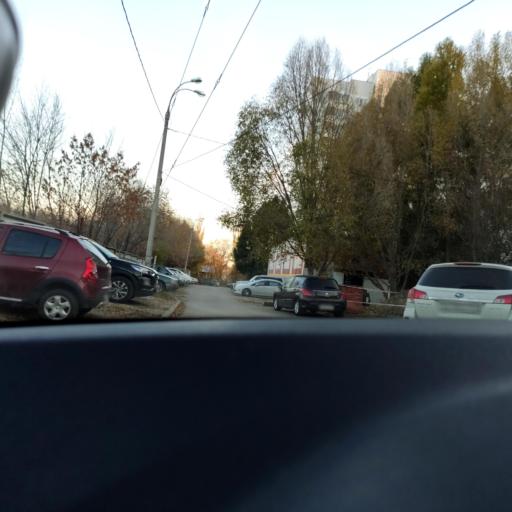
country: RU
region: Samara
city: Samara
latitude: 53.2207
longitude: 50.2333
